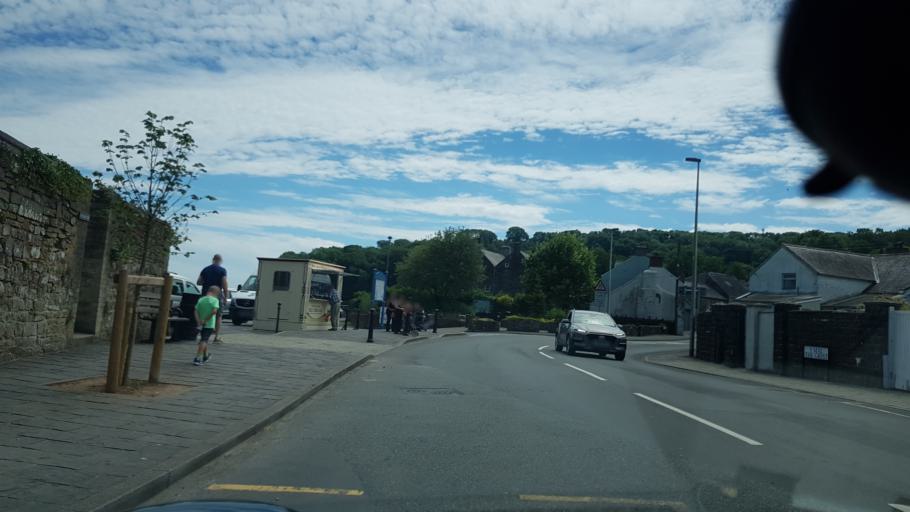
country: GB
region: Wales
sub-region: Carmarthenshire
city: Saint Clears
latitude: 51.7692
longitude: -4.4637
